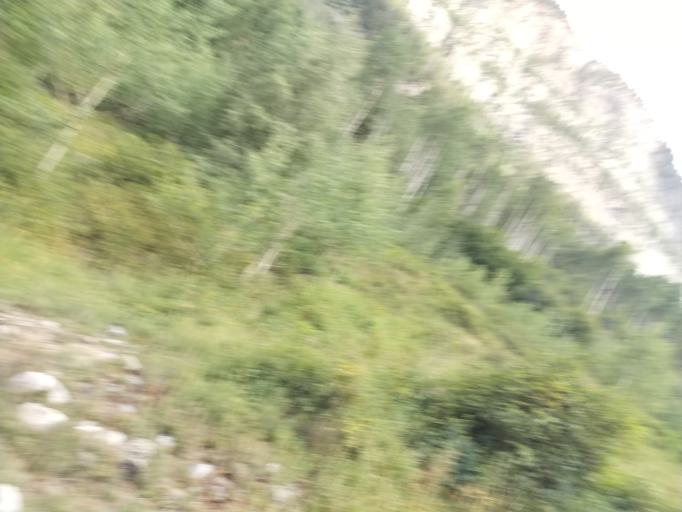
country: US
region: Colorado
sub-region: Gunnison County
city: Crested Butte
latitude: 39.0573
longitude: -107.1092
